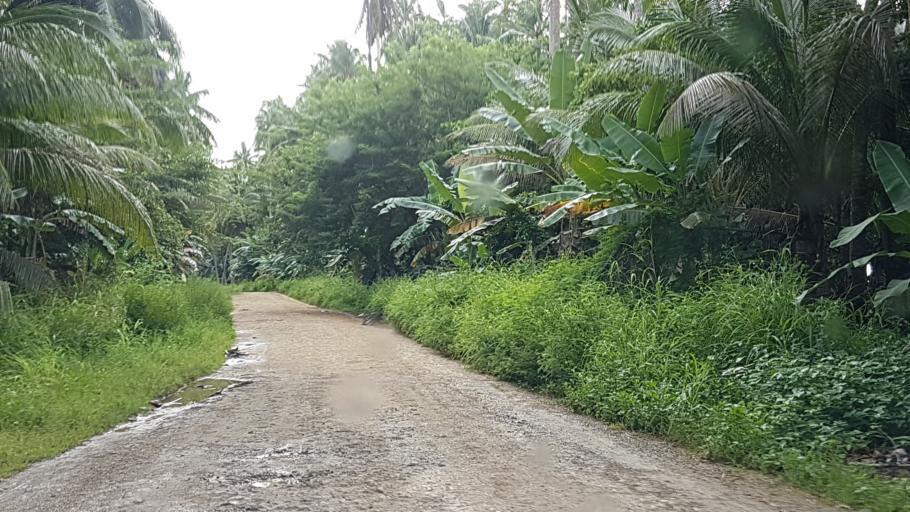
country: PG
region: Milne Bay
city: Alotau
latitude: -10.2794
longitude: 150.7847
